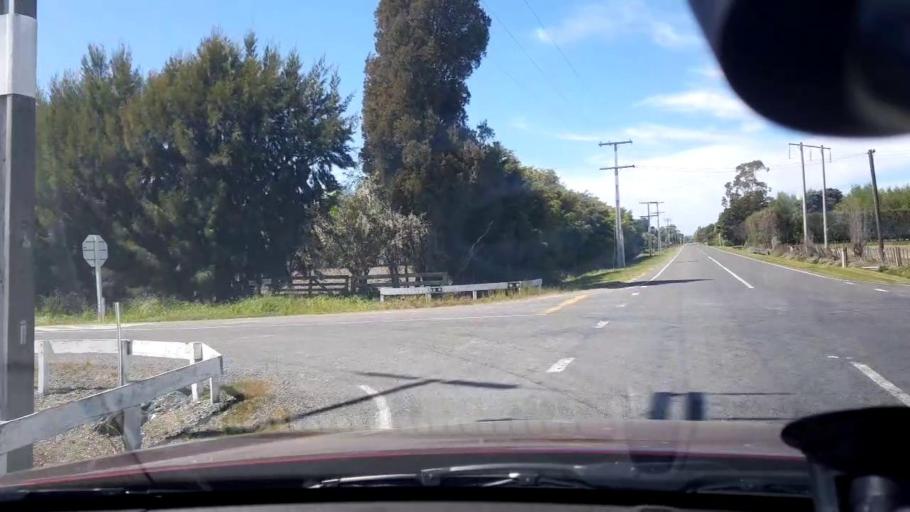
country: NZ
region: Gisborne
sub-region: Gisborne District
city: Gisborne
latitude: -38.6413
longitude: 177.9363
